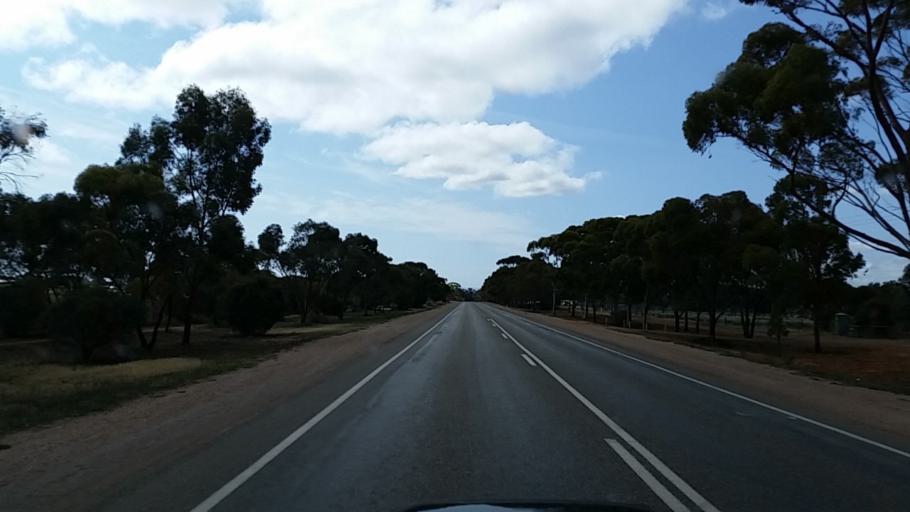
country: AU
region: South Australia
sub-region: Port Pirie City and Dists
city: Port Pirie
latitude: -33.2128
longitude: 138.0107
